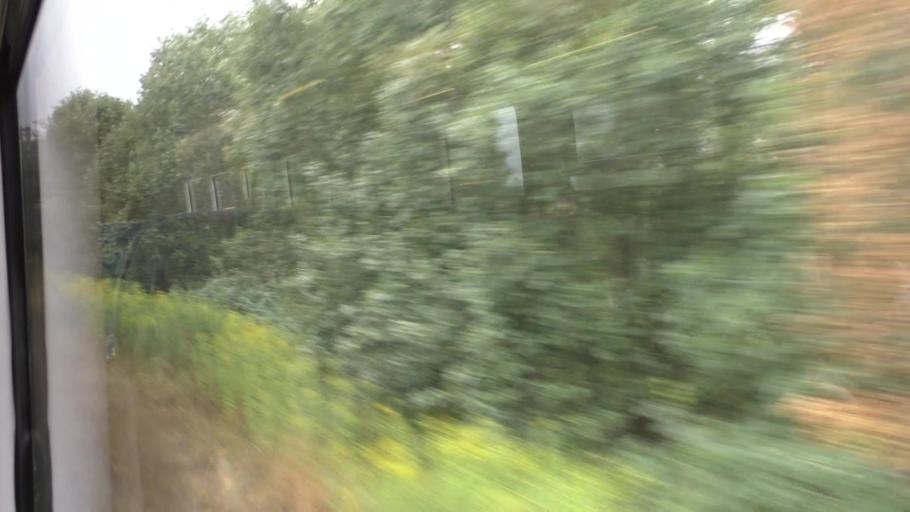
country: DE
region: Saxony
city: Goerlitz
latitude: 51.0849
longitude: 14.9715
